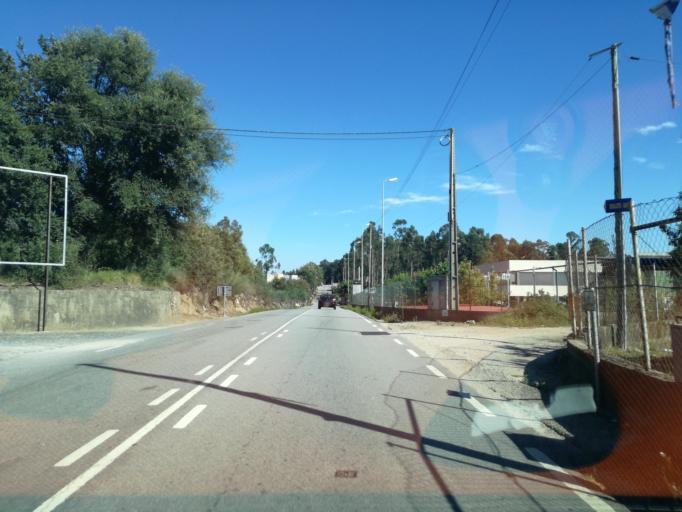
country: PT
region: Porto
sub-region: Trofa
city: Sao Romao do Coronado
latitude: 41.2849
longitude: -8.5912
